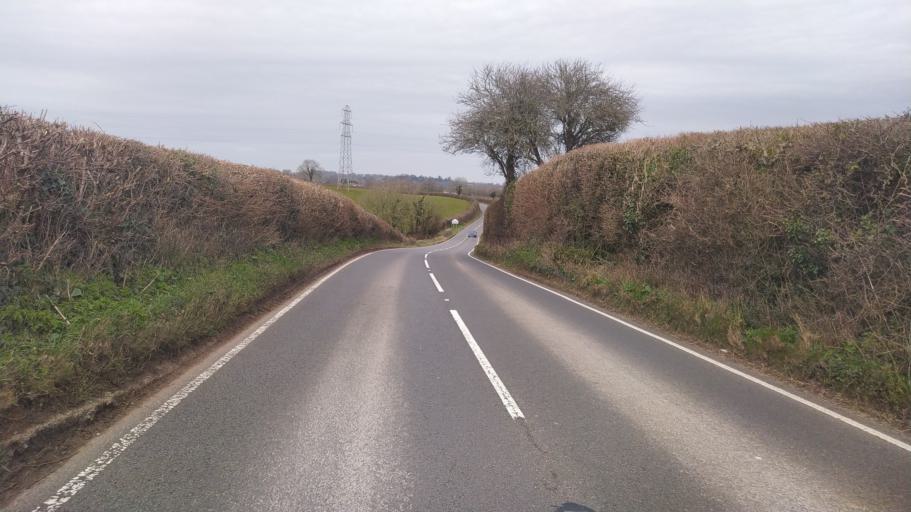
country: GB
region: England
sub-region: Somerset
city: Crewkerne
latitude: 50.8635
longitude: -2.7593
